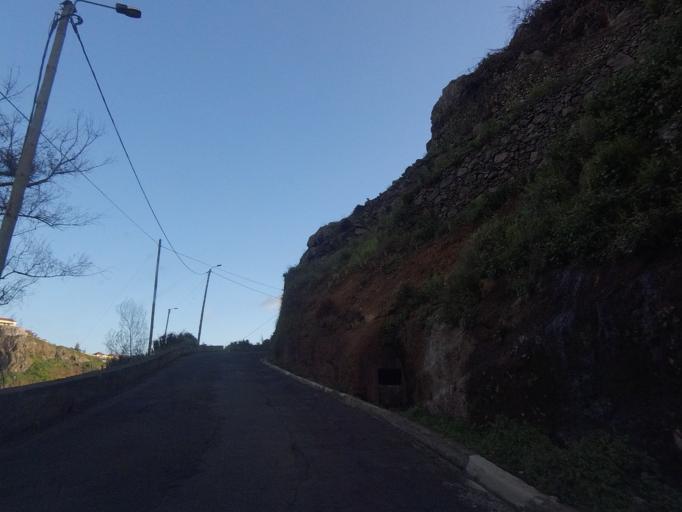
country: PT
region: Madeira
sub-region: Funchal
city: Nossa Senhora do Monte
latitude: 32.6724
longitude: -16.9185
